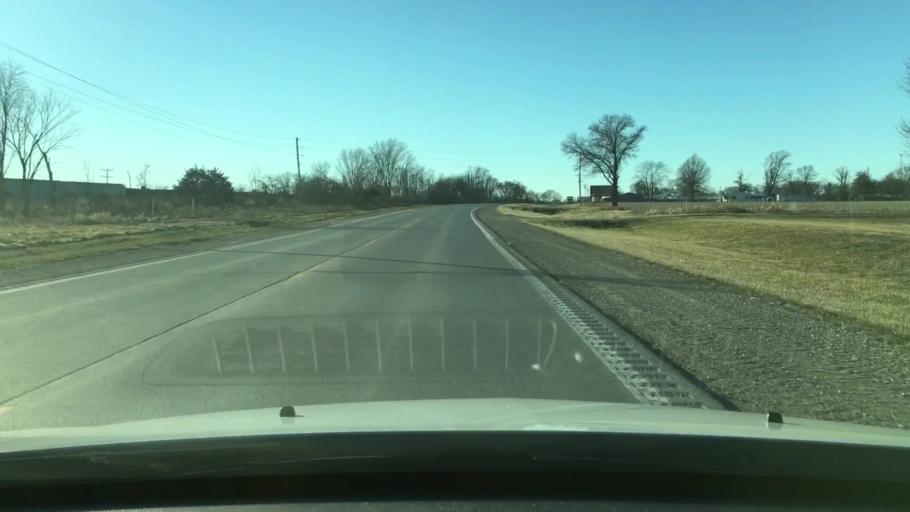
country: US
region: Missouri
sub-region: Audrain County
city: Mexico
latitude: 39.1899
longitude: -91.9863
